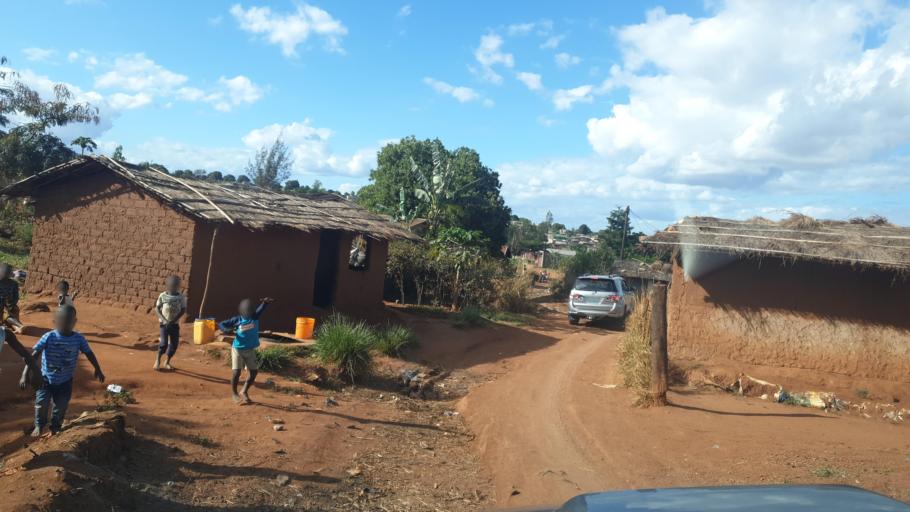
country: MZ
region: Nampula
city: Nampula
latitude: -15.0903
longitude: 39.2255
